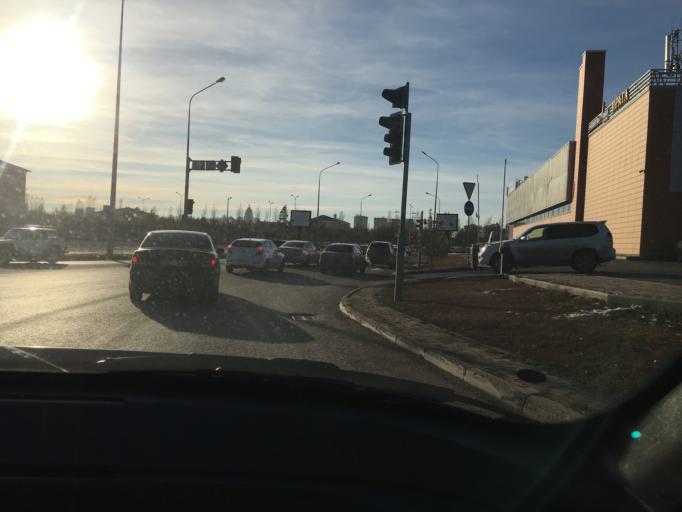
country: KZ
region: Astana Qalasy
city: Astana
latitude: 51.1486
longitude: 71.4468
